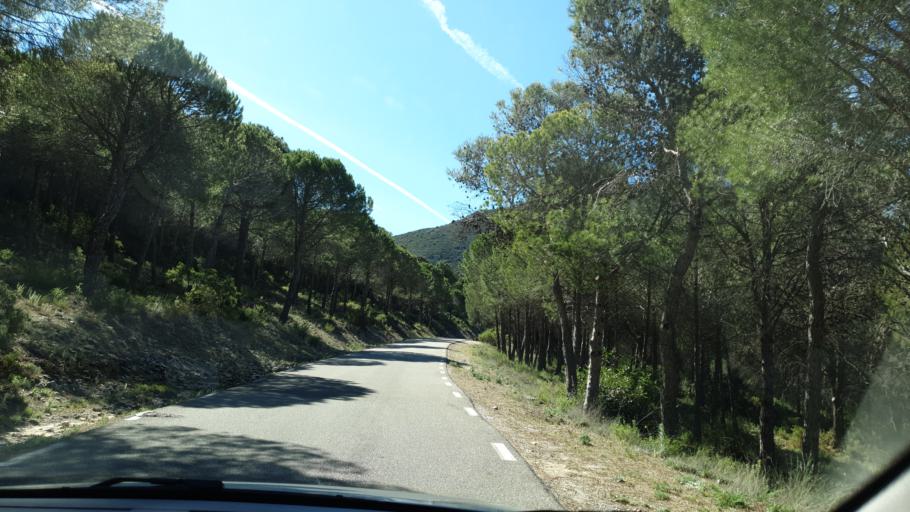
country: ES
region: Andalusia
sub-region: Provincia de Malaga
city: Ojen
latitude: 36.5926
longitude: -4.8574
